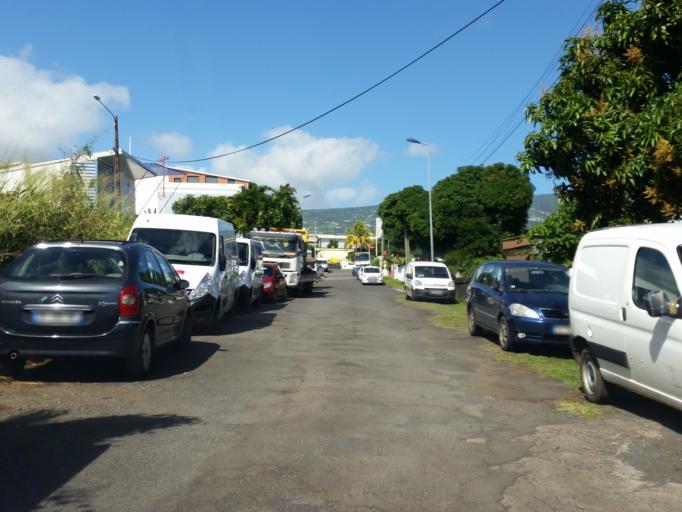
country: RE
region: Reunion
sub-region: Reunion
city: Sainte-Marie
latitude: -20.8958
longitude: 55.5324
